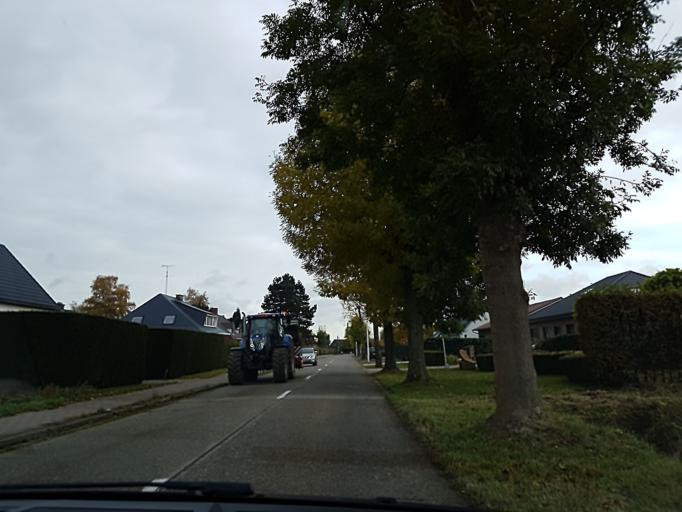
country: BE
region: Flanders
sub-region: Provincie Antwerpen
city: Boechout
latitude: 51.1609
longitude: 4.5181
